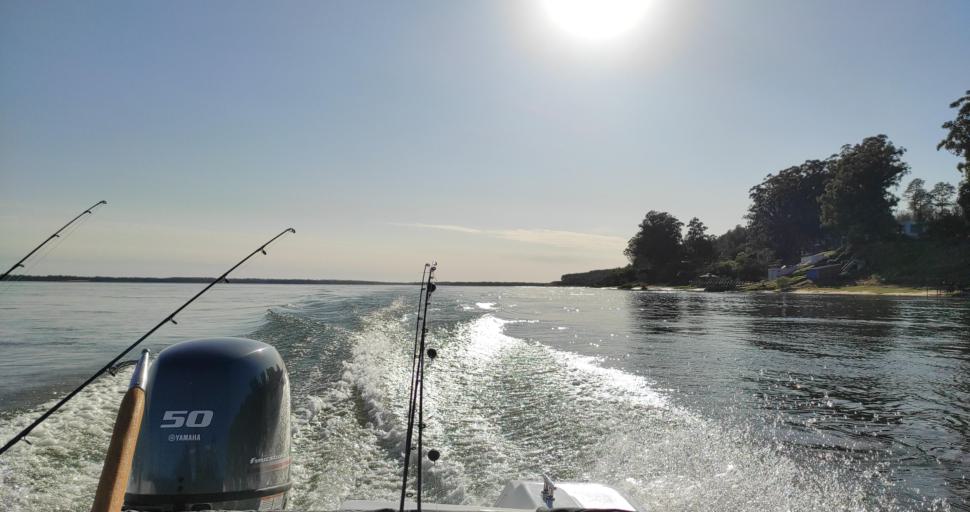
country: AR
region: Corrientes
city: Ituzaingo
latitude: -27.5971
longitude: -56.8143
